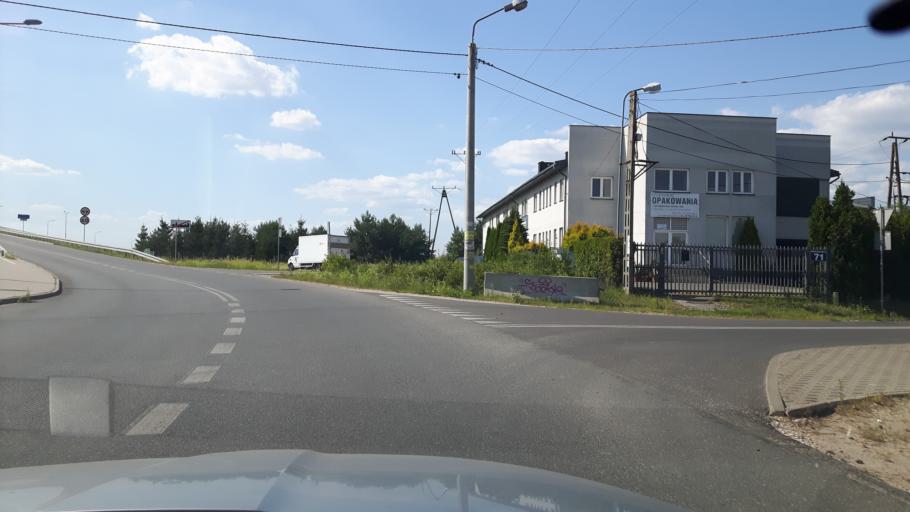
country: PL
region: Masovian Voivodeship
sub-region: Powiat pruszkowski
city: Nowe Grocholice
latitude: 52.1640
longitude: 20.9110
